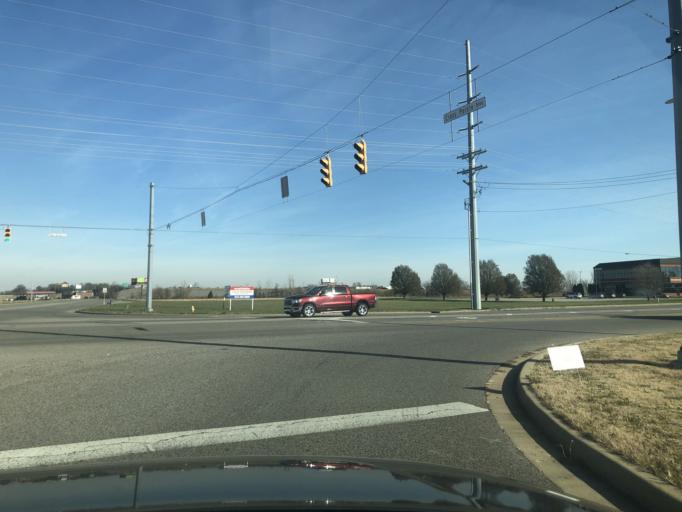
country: US
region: Indiana
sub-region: Vanderburgh County
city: Melody Hill
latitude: 37.9909
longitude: -87.4671
